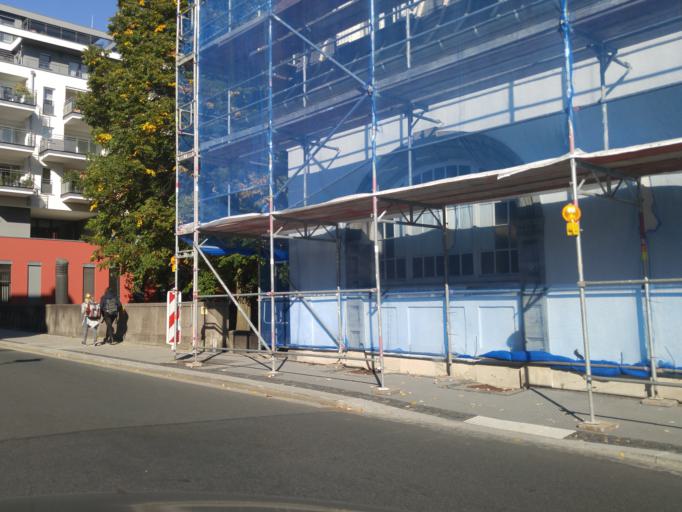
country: DE
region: Hesse
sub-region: Regierungsbezirk Darmstadt
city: Bad Nauheim
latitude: 50.3636
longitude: 8.7407
